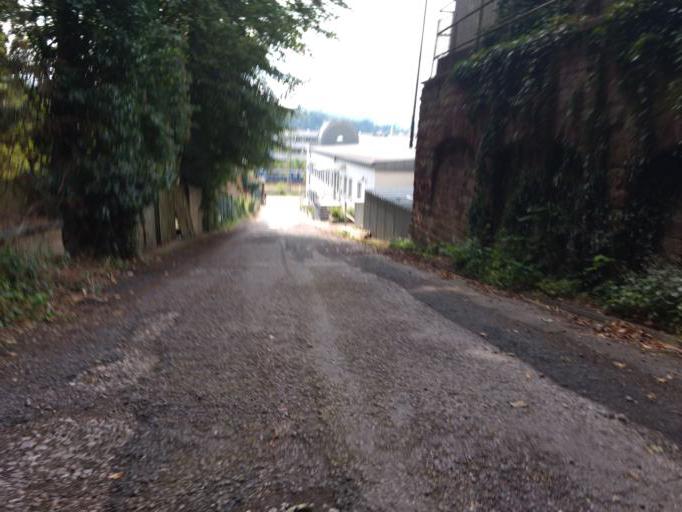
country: DE
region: Saarland
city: Merzig
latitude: 49.4343
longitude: 6.6360
